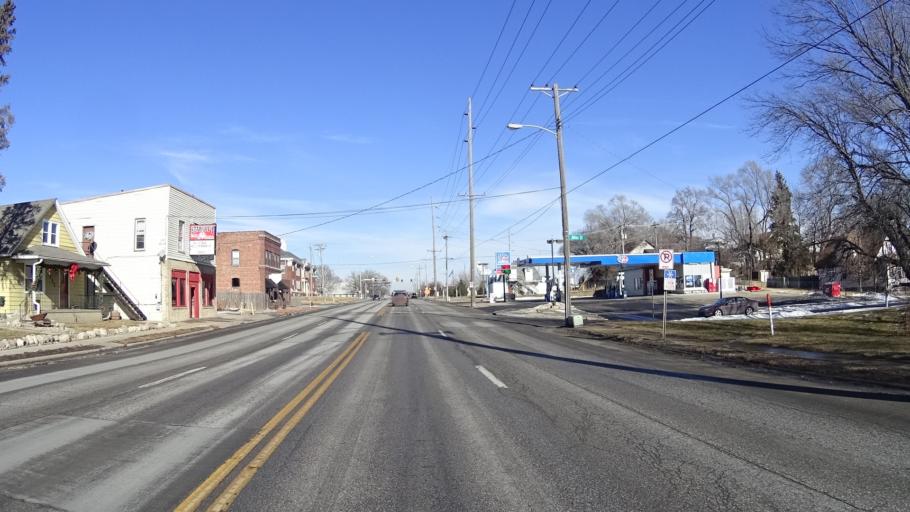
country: US
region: Nebraska
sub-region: Douglas County
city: Omaha
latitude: 41.2216
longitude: -95.9333
